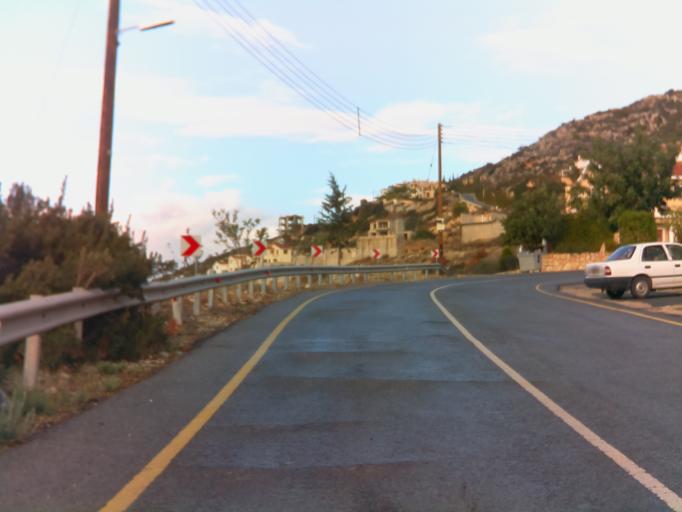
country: CY
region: Pafos
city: Pegeia
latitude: 34.8856
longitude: 32.3776
